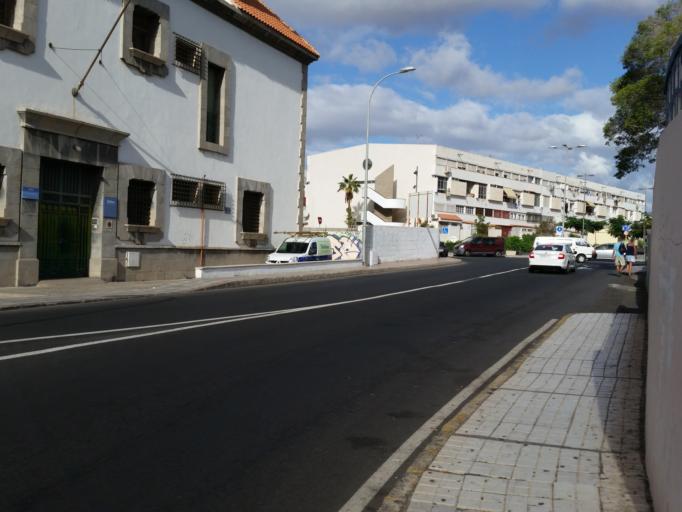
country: ES
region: Canary Islands
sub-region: Provincia de Las Palmas
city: Playa del Ingles
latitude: 27.7650
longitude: -15.5741
